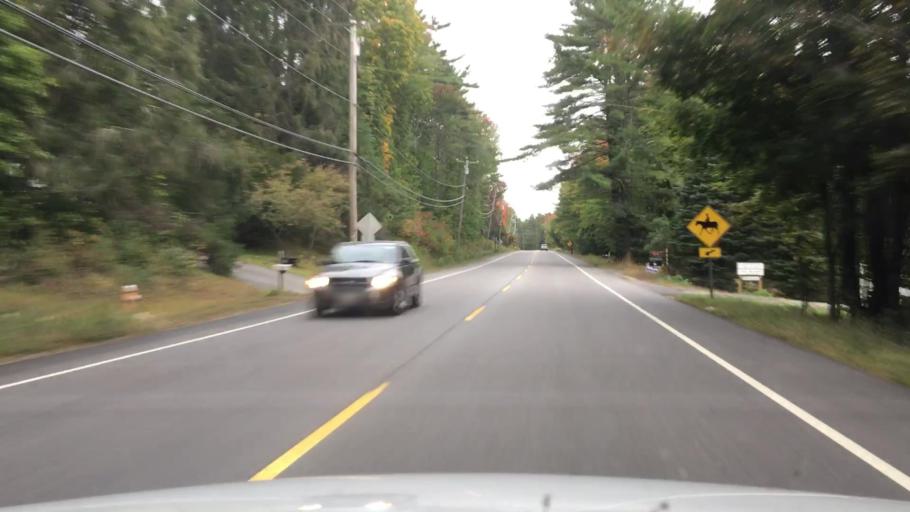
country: US
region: Maine
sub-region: Cumberland County
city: New Gloucester
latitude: 43.9127
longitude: -70.3520
